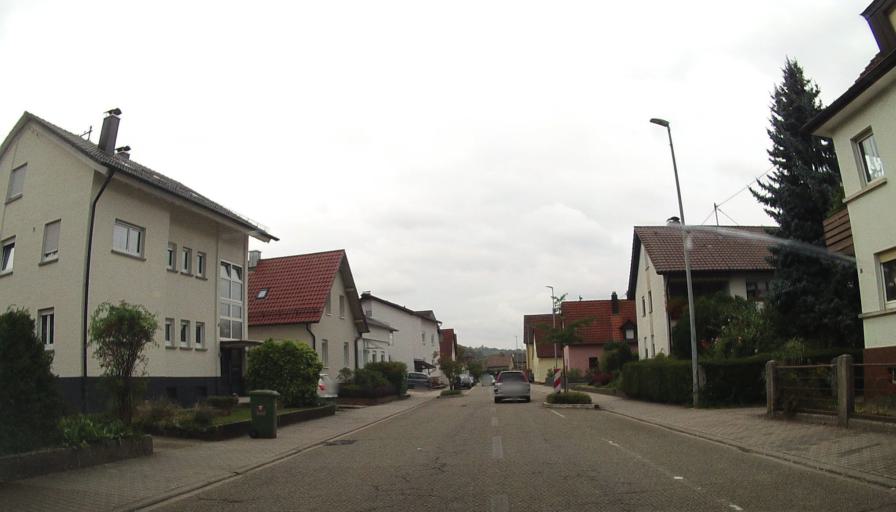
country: DE
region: Baden-Wuerttemberg
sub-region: Karlsruhe Region
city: Gaggenau
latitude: 48.8112
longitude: 8.3149
